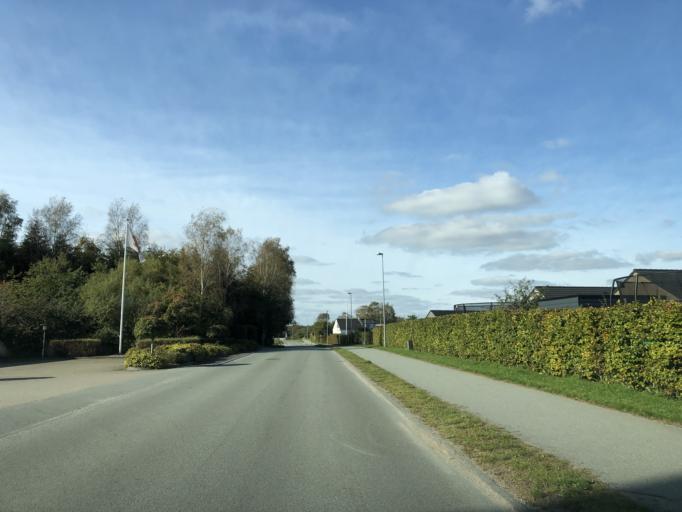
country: DK
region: Central Jutland
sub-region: Syddjurs Kommune
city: Hornslet
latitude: 56.3127
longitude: 10.3067
